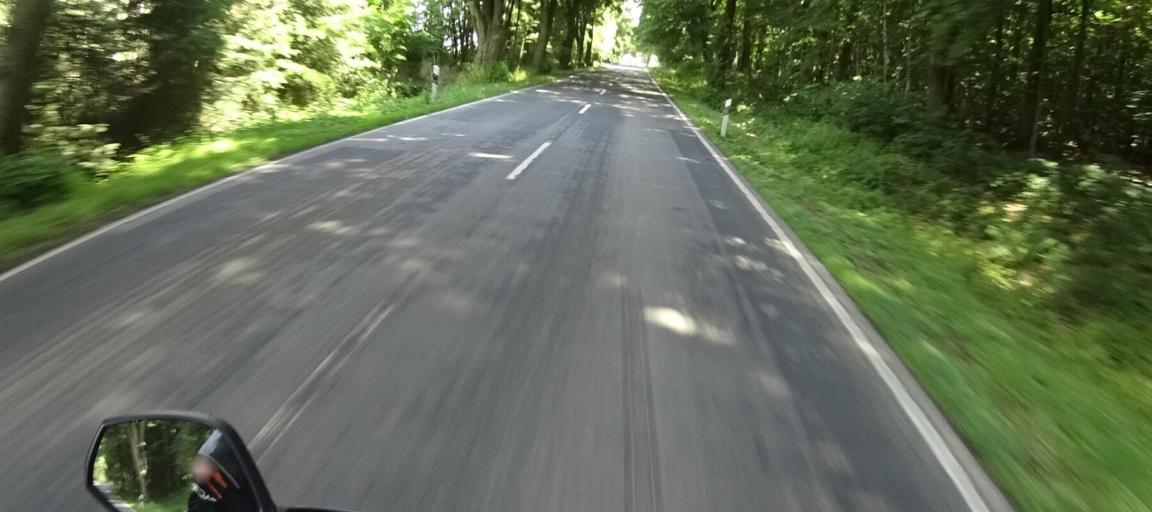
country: DE
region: Lower Saxony
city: Holzminden
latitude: 51.7909
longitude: 9.4431
